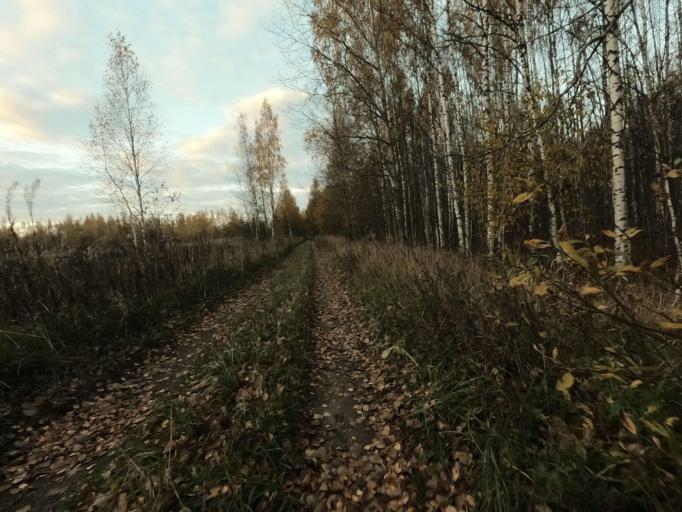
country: RU
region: Leningrad
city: Mga
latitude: 59.8217
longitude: 31.1780
